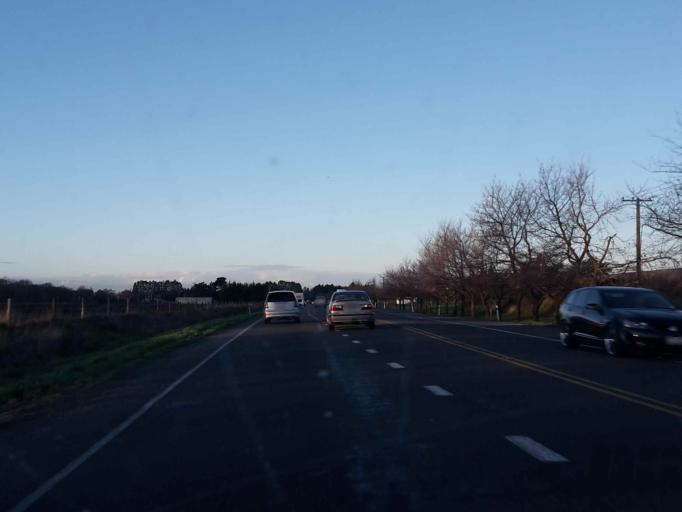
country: NZ
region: Canterbury
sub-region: Selwyn District
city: Rolleston
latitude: -43.5852
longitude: 172.3939
